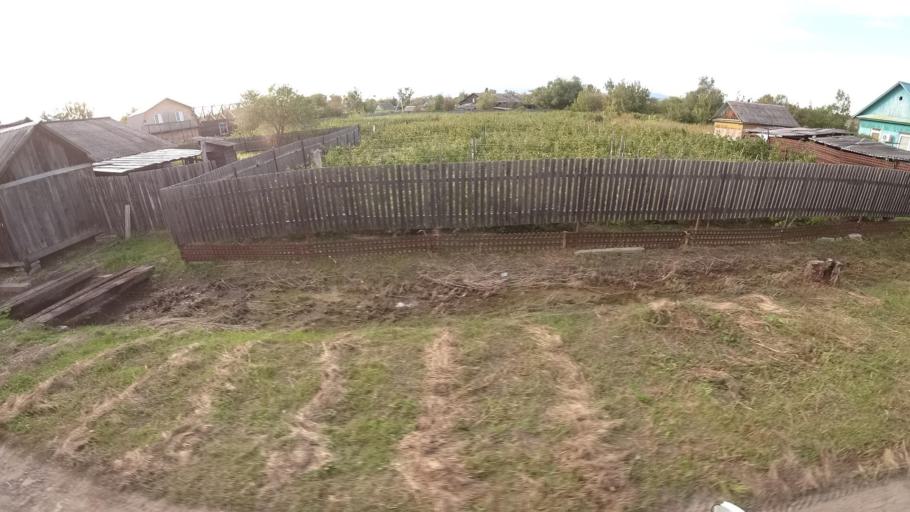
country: RU
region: Primorskiy
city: Dostoyevka
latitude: 44.2880
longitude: 133.4301
